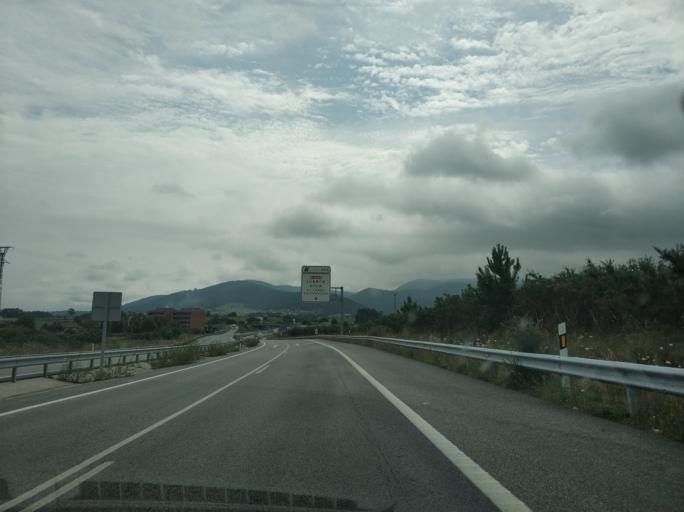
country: ES
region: Asturias
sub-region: Province of Asturias
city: Navia
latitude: 43.5287
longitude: -6.5592
